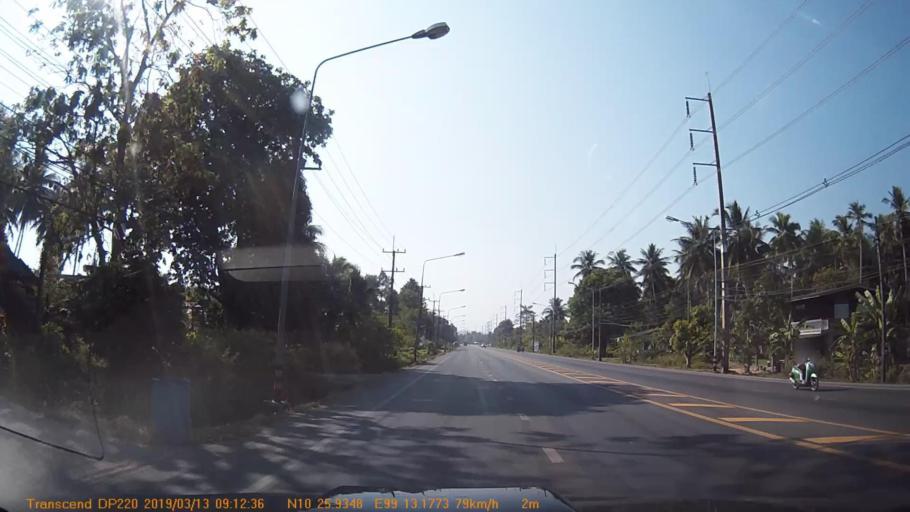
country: TH
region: Chumphon
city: Chumphon
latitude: 10.4319
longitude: 99.2198
